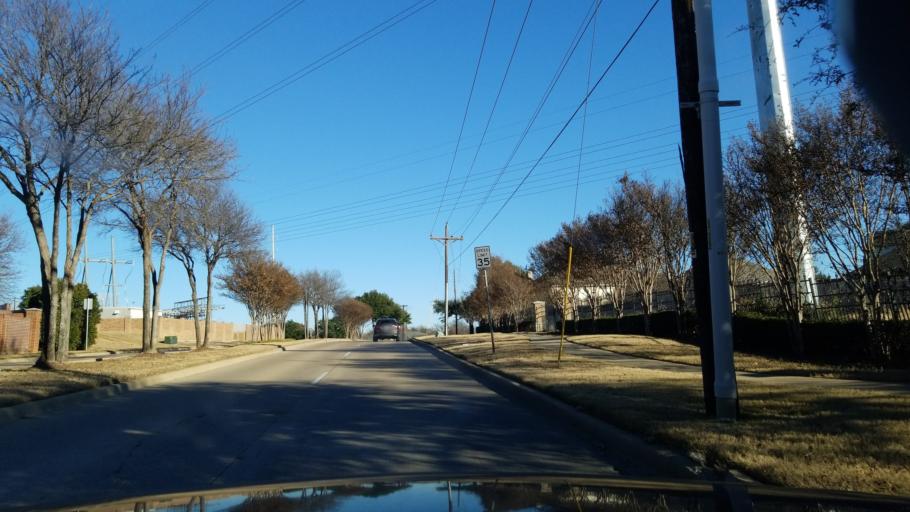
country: US
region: Texas
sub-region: Denton County
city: Corinth
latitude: 33.1581
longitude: -97.0900
